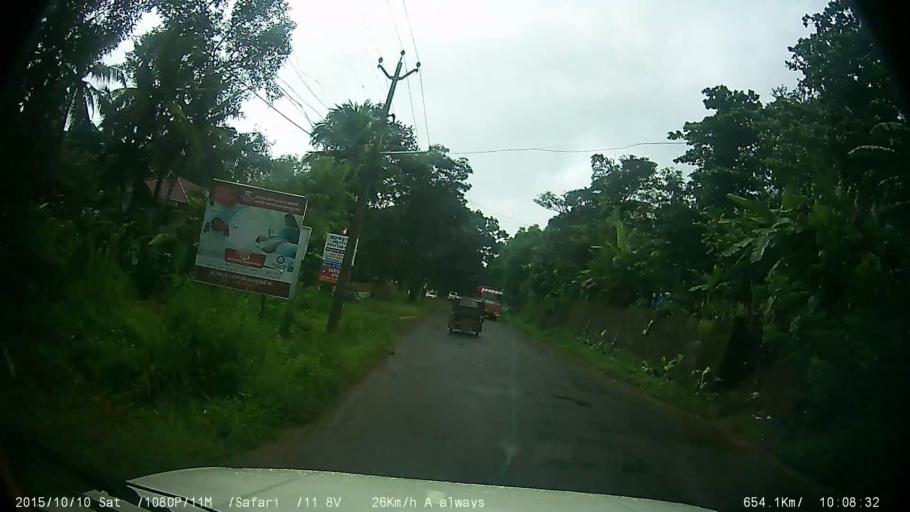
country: IN
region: Kerala
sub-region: Kottayam
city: Kottayam
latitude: 9.6379
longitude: 76.5300
